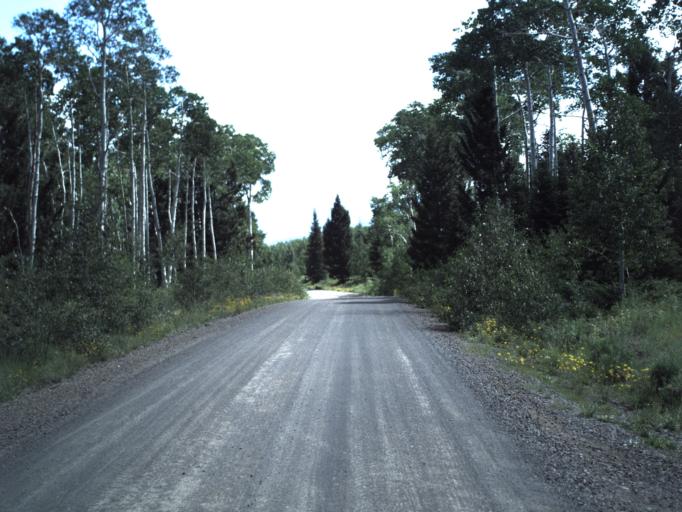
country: US
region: Utah
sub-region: Piute County
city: Junction
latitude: 38.2546
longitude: -112.3320
